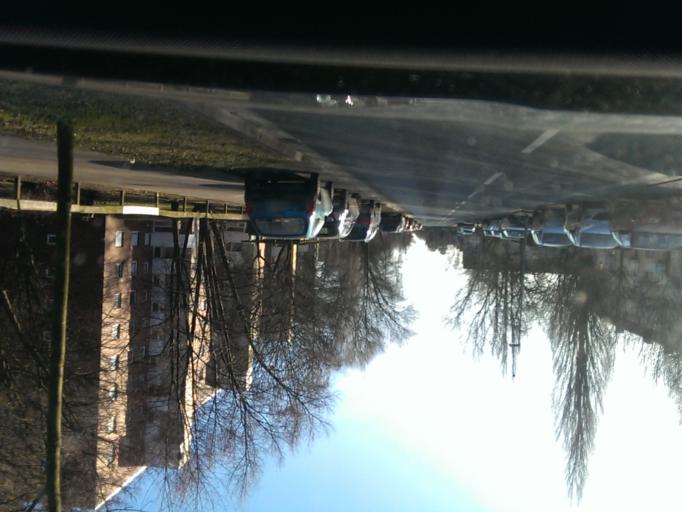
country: DE
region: Lower Saxony
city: Langenhagen
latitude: 52.4175
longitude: 9.7816
